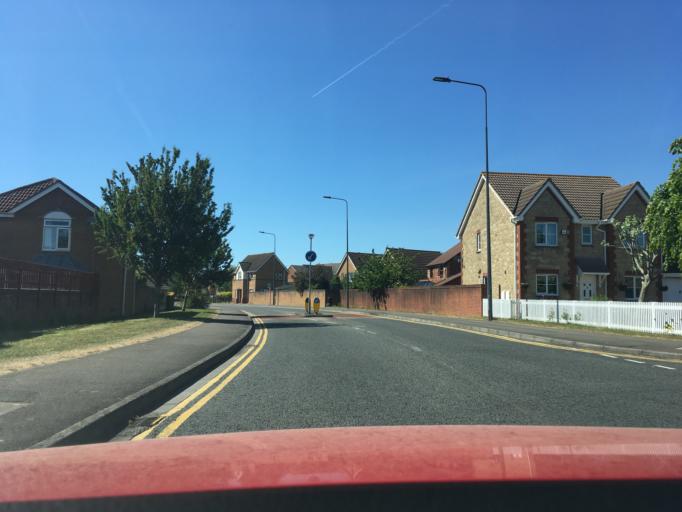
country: GB
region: England
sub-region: South Gloucestershire
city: Stoke Gifford
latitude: 51.5281
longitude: -2.5340
